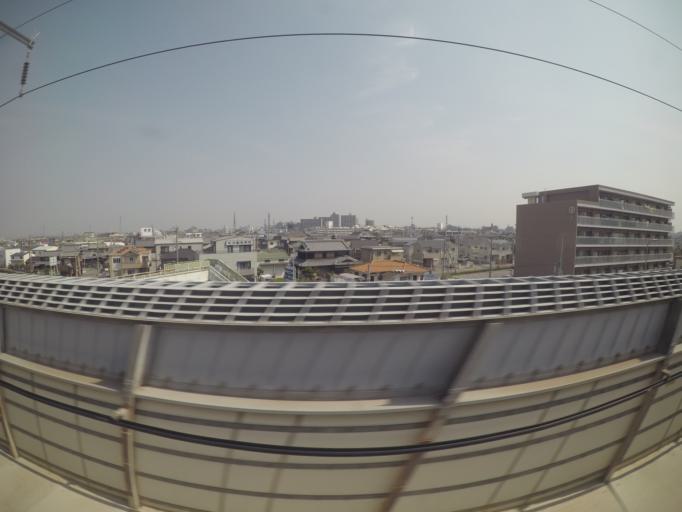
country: JP
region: Hyogo
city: Kakogawacho-honmachi
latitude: 34.7075
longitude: 134.8841
